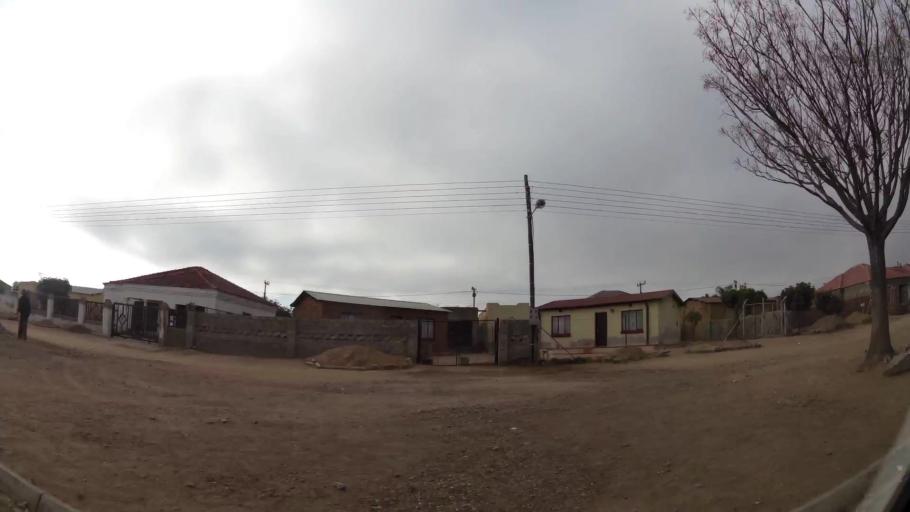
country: ZA
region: Limpopo
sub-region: Capricorn District Municipality
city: Polokwane
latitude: -23.8371
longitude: 29.3814
